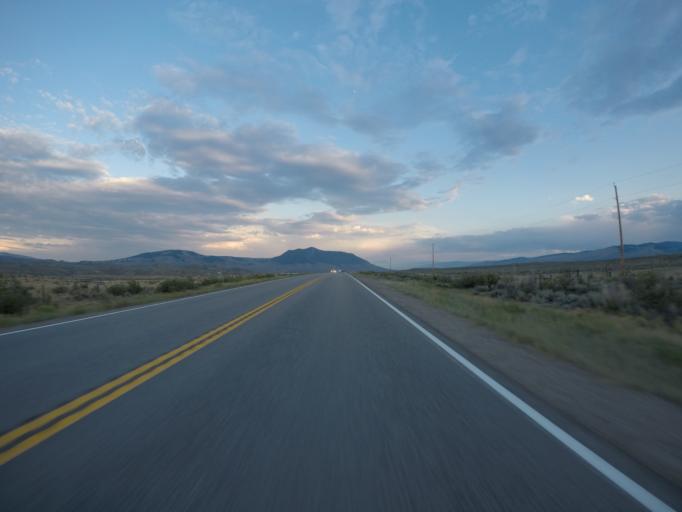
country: US
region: Colorado
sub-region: Grand County
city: Kremmling
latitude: 40.1698
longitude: -106.4178
